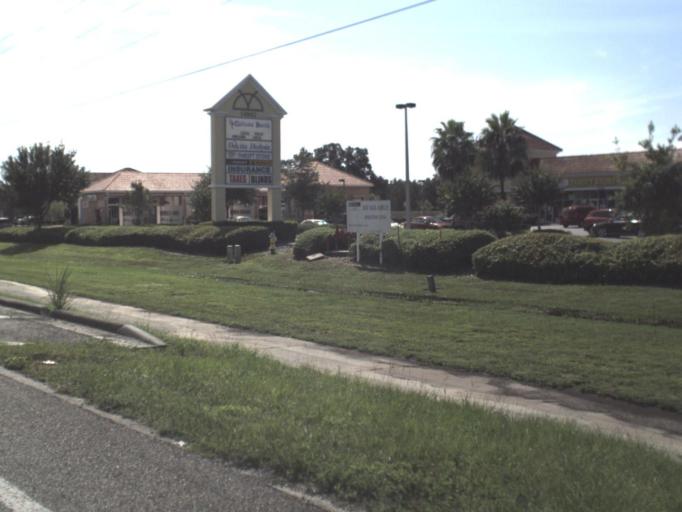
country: US
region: Florida
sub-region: Sarasota County
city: North Port
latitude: 27.0390
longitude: -82.2227
